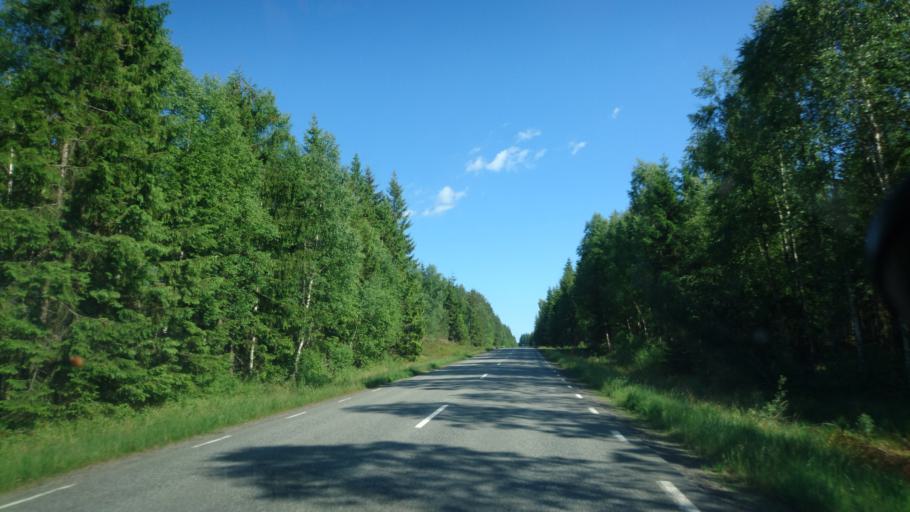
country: SE
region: Skane
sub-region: Osby Kommun
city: Lonsboda
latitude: 56.4386
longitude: 14.2494
